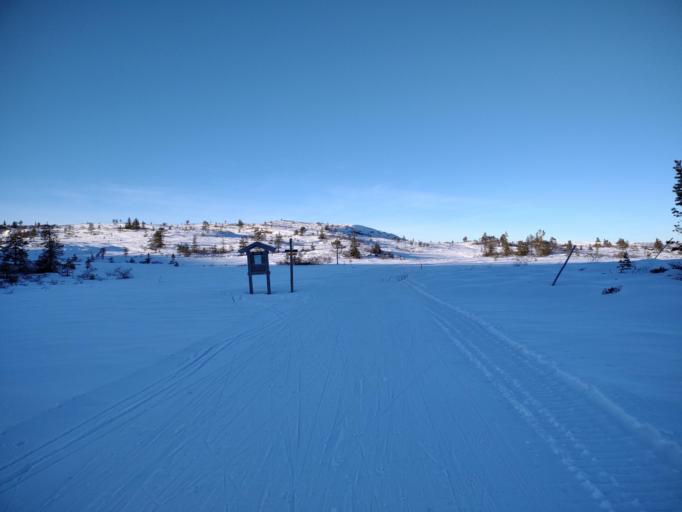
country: NO
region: Buskerud
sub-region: Rollag
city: Rollag
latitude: 59.8133
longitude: 9.3152
